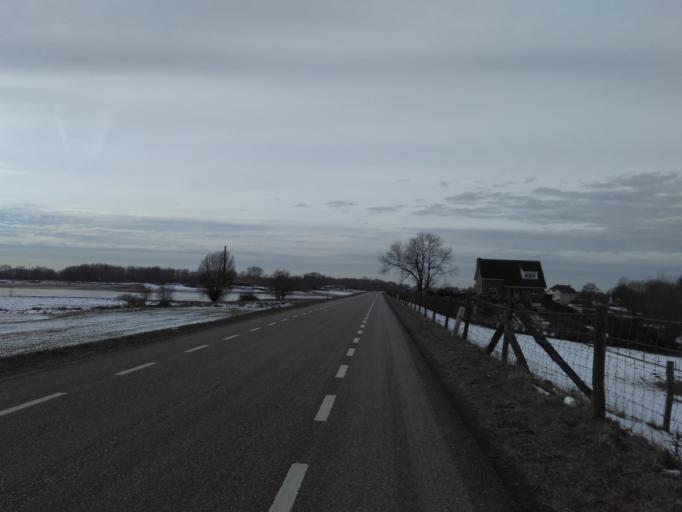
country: NL
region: Gelderland
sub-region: Gemeente Overbetuwe
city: Oosterhout
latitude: 51.8754
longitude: 5.8152
